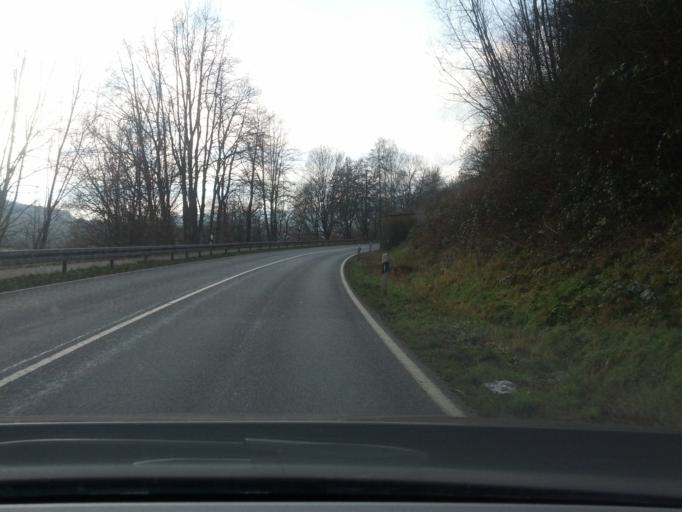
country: DE
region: Lower Saxony
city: Buhren
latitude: 51.4665
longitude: 9.6403
